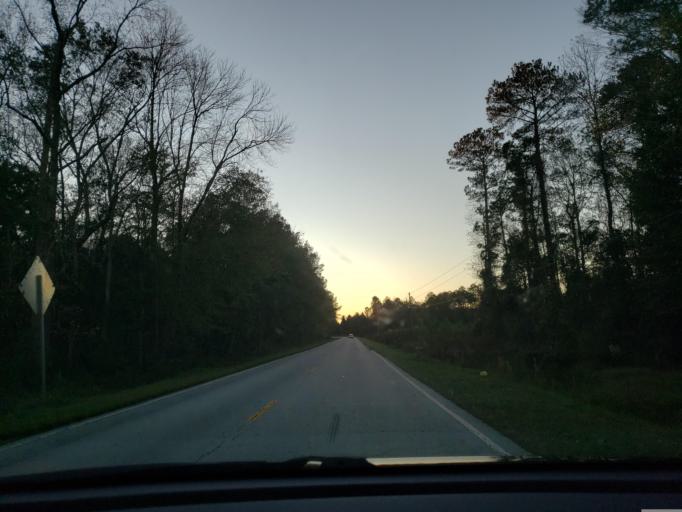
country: US
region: North Carolina
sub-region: Onslow County
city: Half Moon
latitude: 34.7336
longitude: -77.5855
